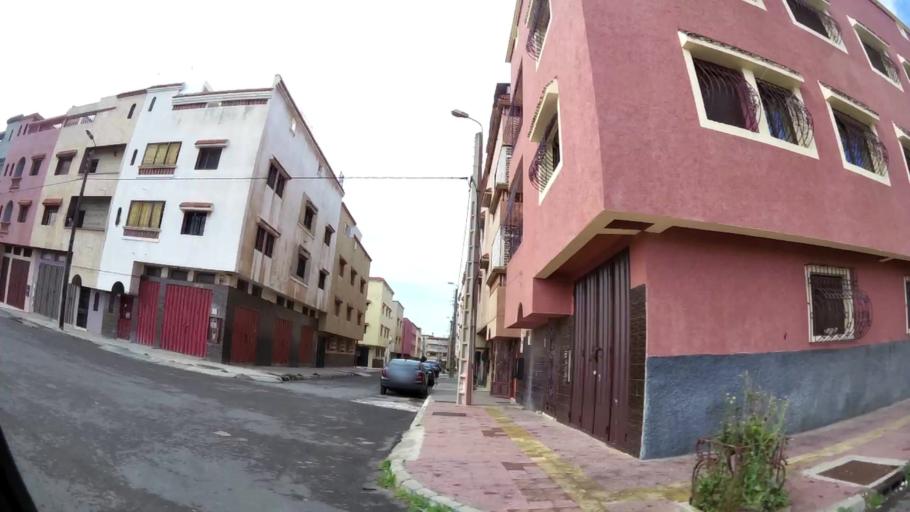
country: MA
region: Grand Casablanca
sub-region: Mohammedia
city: Mohammedia
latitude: 33.6808
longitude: -7.3800
